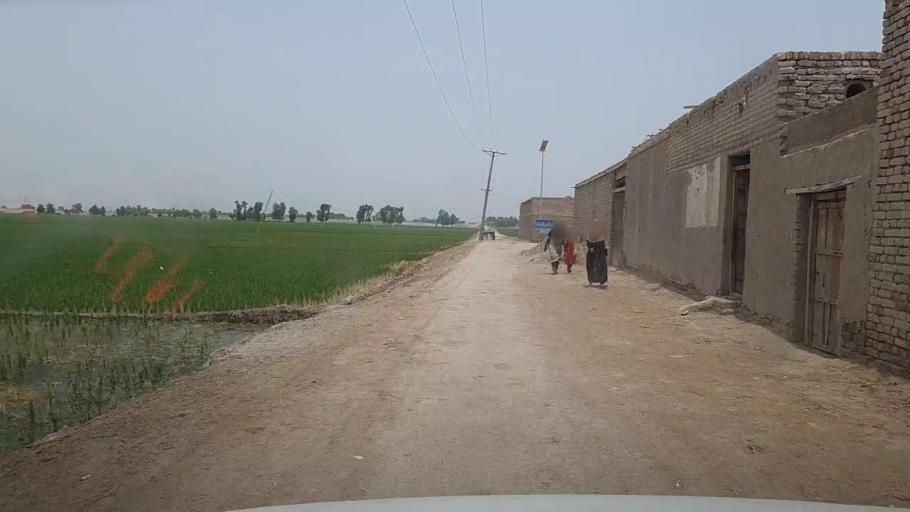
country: PK
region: Sindh
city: Sita Road
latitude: 27.0435
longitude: 67.8465
